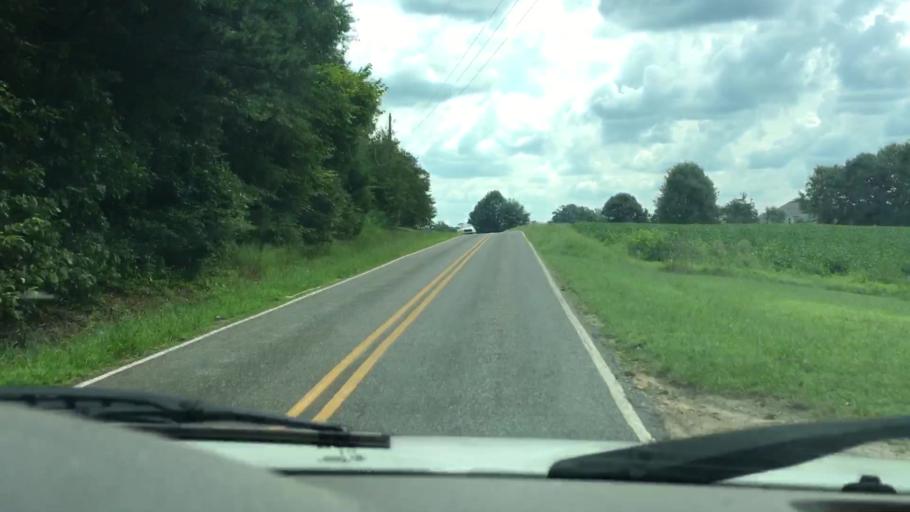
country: US
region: North Carolina
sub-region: Iredell County
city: Troutman
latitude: 35.6682
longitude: -80.8322
